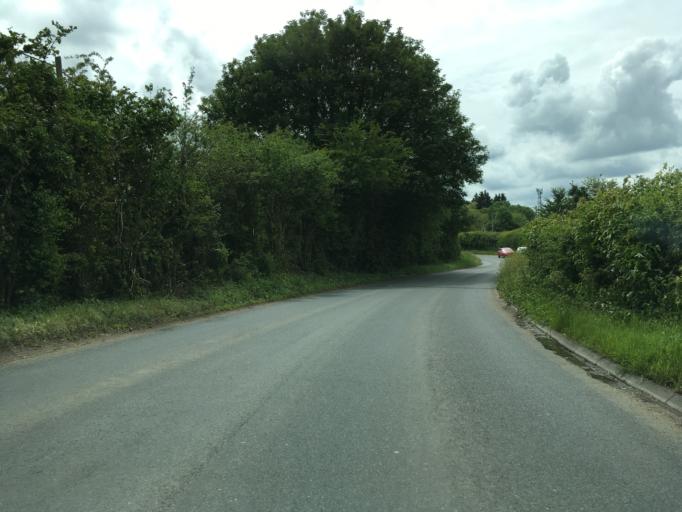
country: GB
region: England
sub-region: Wiltshire
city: Purton
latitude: 51.5665
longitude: -1.8891
